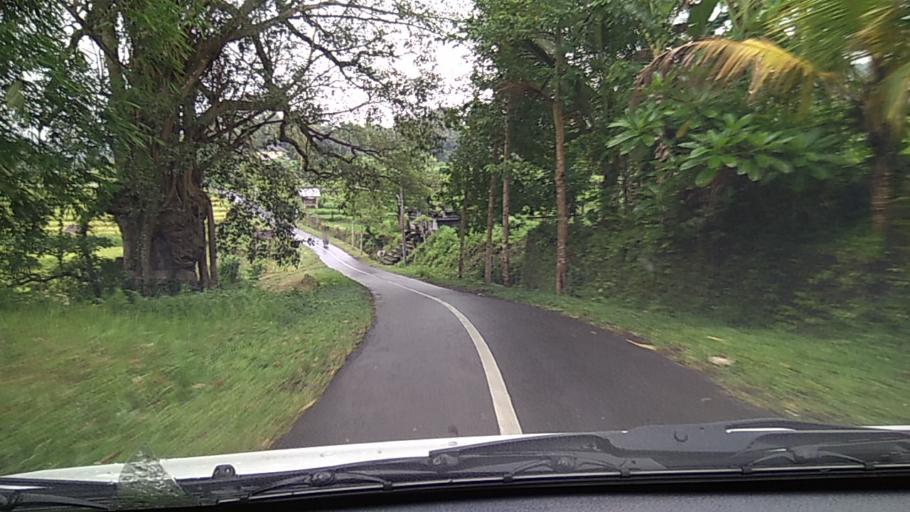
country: ID
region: Bali
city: Tiyingtali Kelod
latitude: -8.4032
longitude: 115.6177
